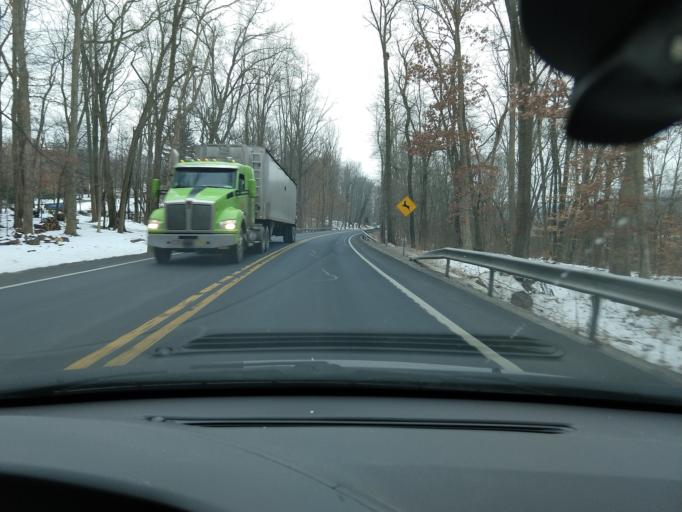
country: US
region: Pennsylvania
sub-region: Lehigh County
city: Macungie
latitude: 40.4567
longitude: -75.5492
